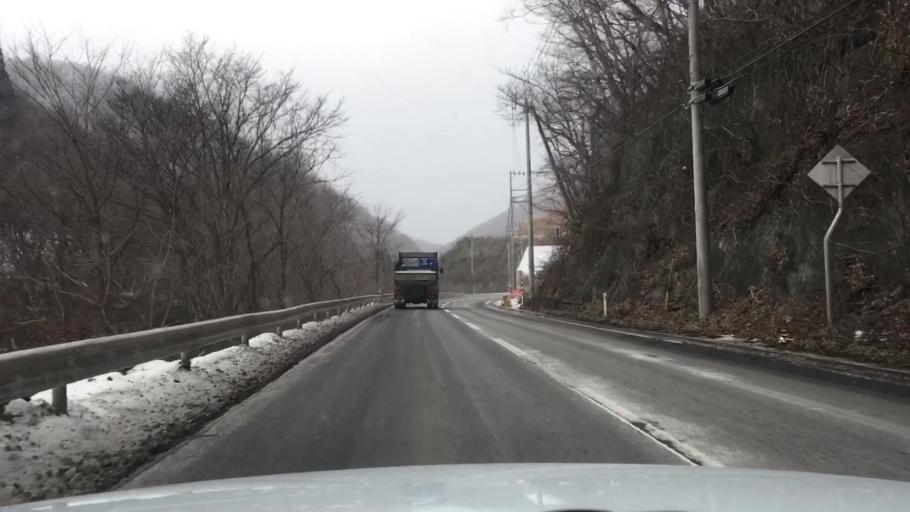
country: JP
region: Iwate
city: Tono
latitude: 39.6223
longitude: 141.4752
